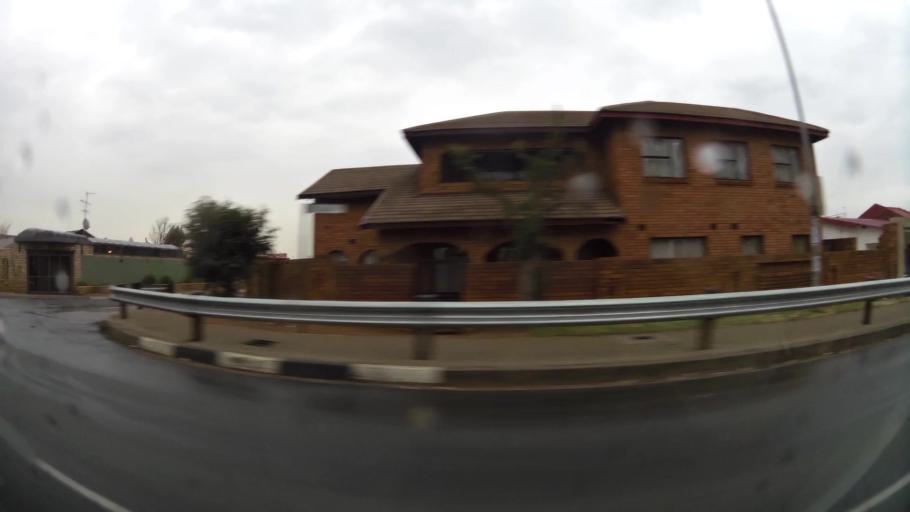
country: ZA
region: Gauteng
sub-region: City of Johannesburg Metropolitan Municipality
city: Soweto
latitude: -26.2644
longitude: 27.8577
